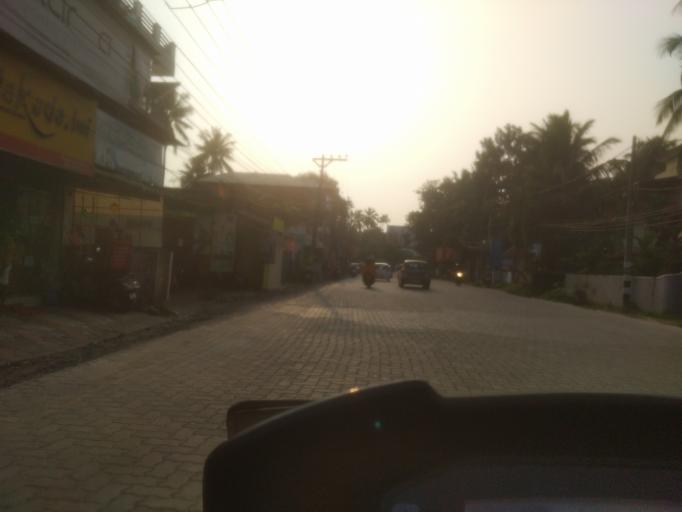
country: IN
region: Kerala
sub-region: Ernakulam
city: Cochin
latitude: 9.9387
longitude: 76.3282
